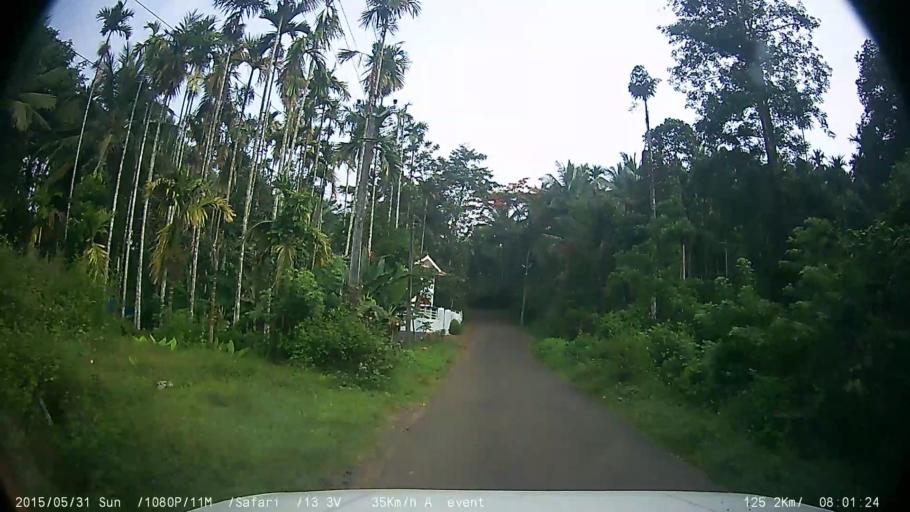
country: IN
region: Kerala
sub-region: Wayanad
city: Kalpetta
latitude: 11.6323
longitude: 76.0468
